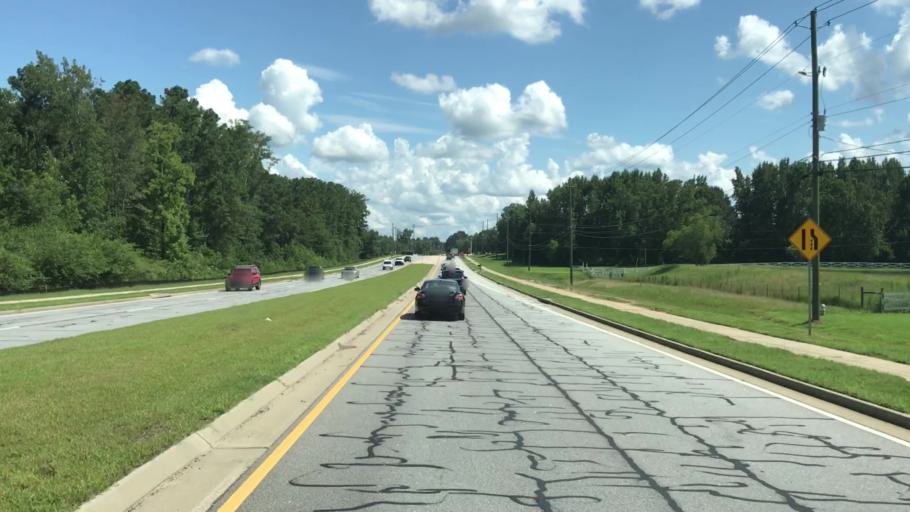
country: US
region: Georgia
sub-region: Walton County
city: Loganville
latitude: 33.8599
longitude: -83.9070
